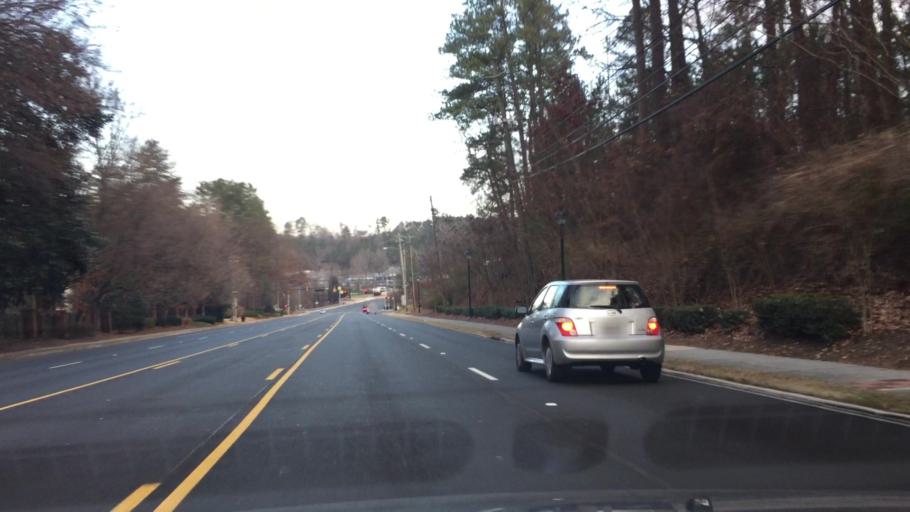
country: US
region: Georgia
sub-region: DeKalb County
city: Dunwoody
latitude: 33.9579
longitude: -84.3649
